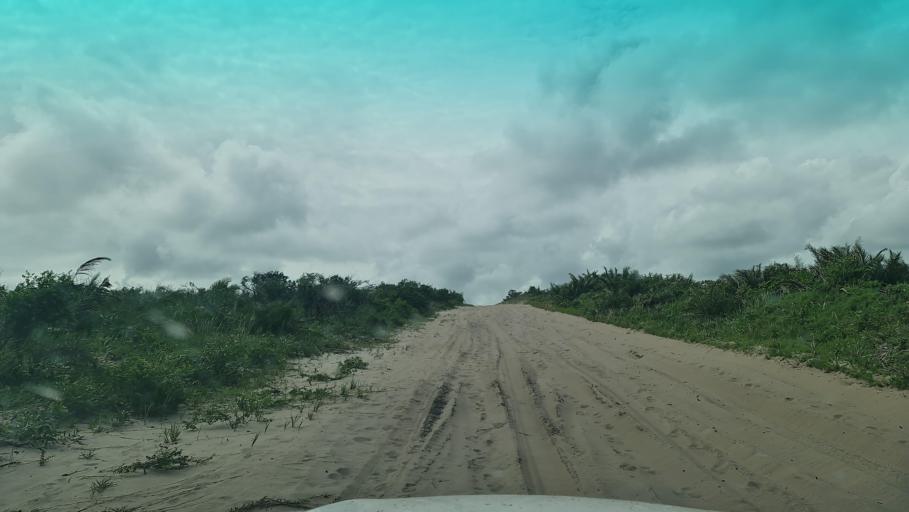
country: MZ
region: Maputo
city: Manhica
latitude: -25.4478
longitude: 32.9517
